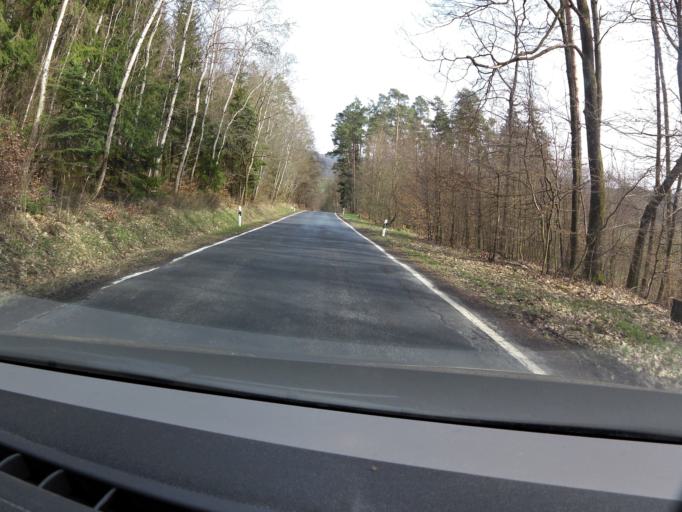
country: DE
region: Thuringia
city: Stadtlengsfeld
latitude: 50.7770
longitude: 10.1121
